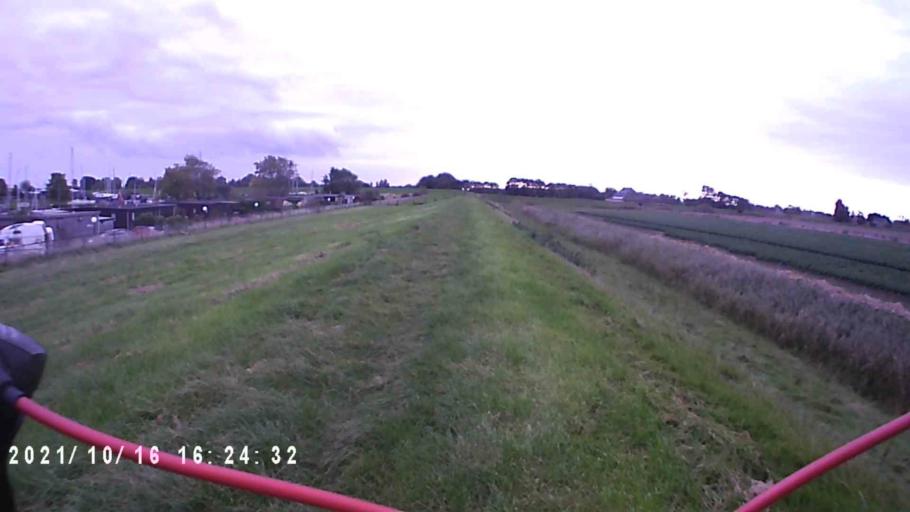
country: NL
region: Friesland
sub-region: Gemeente Dongeradeel
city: Anjum
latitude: 53.3845
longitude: 6.1564
